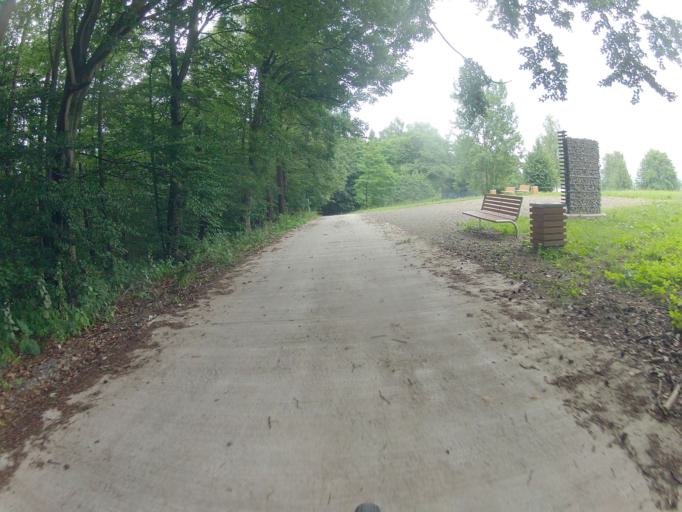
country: PL
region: Lesser Poland Voivodeship
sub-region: Powiat nowosadecki
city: Stary Sacz
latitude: 49.5622
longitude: 20.6254
